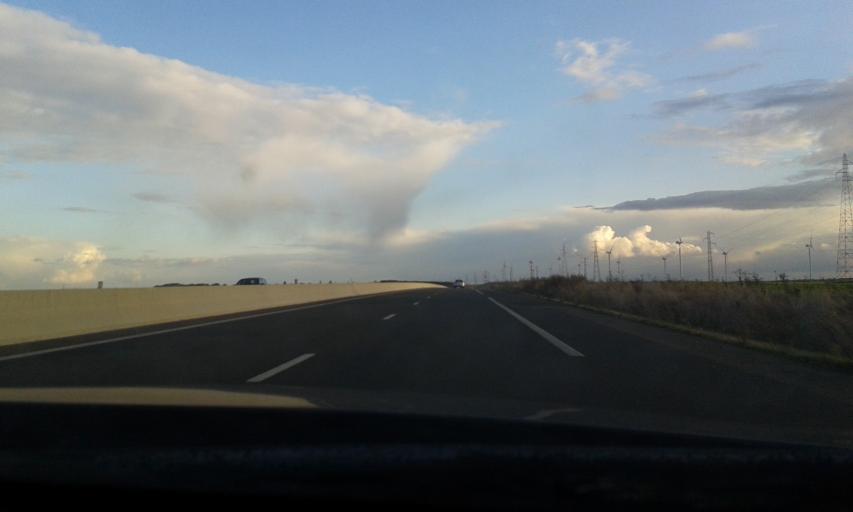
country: FR
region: Centre
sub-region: Departement d'Eure-et-Loir
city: Voves
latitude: 48.3423
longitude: 1.6331
